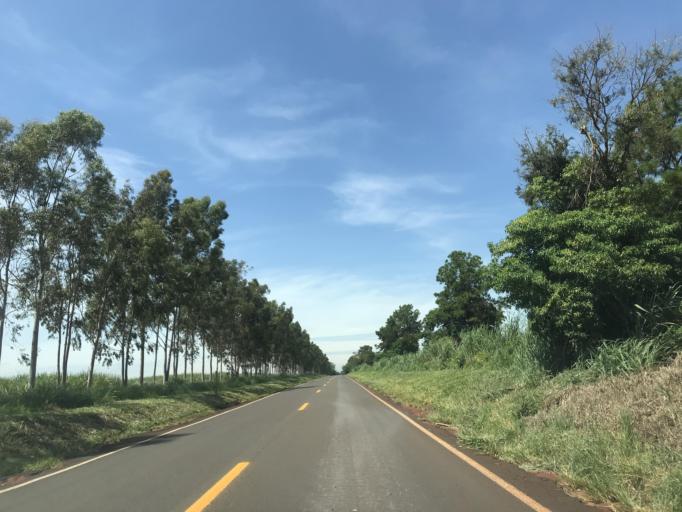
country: BR
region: Parana
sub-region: Paranavai
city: Nova Aurora
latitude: -22.8319
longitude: -52.6560
